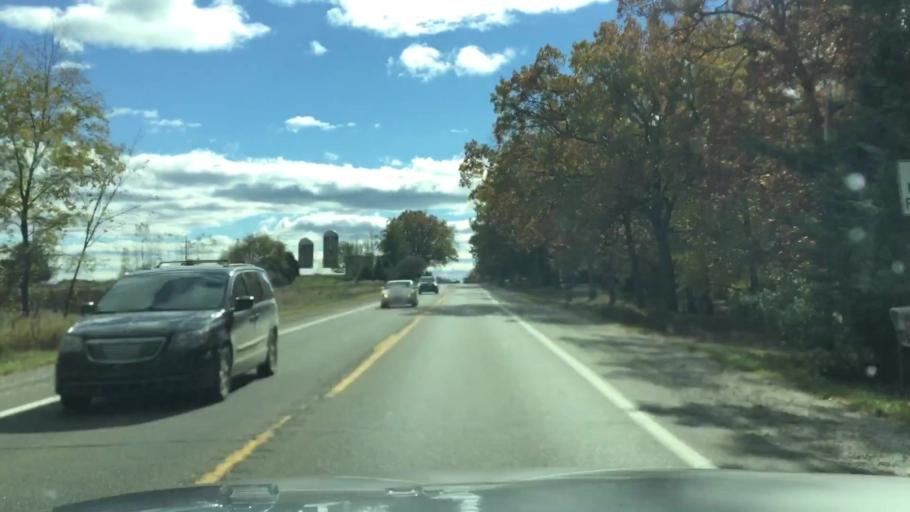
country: US
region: Michigan
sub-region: Lapeer County
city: Barnes Lake-Millers Lake
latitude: 43.1535
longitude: -83.3114
